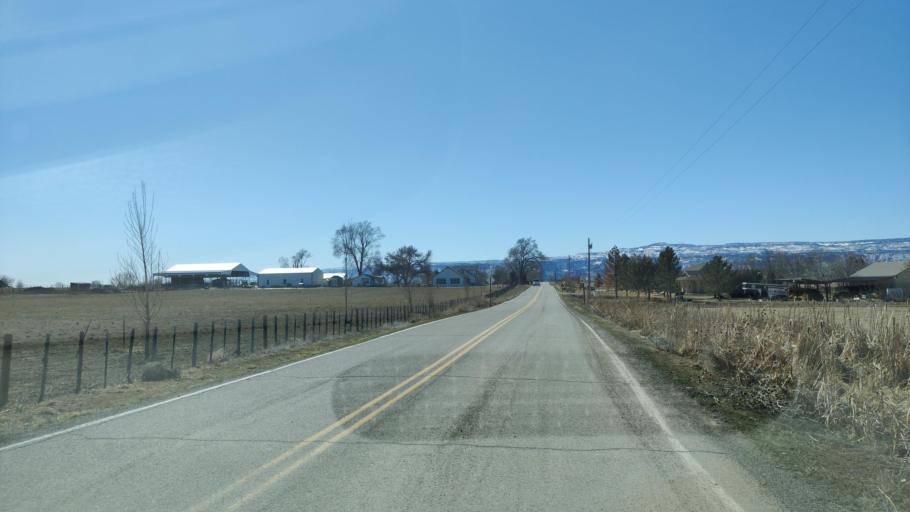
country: US
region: Colorado
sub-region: Mesa County
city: Fruita
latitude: 39.1860
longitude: -108.7197
